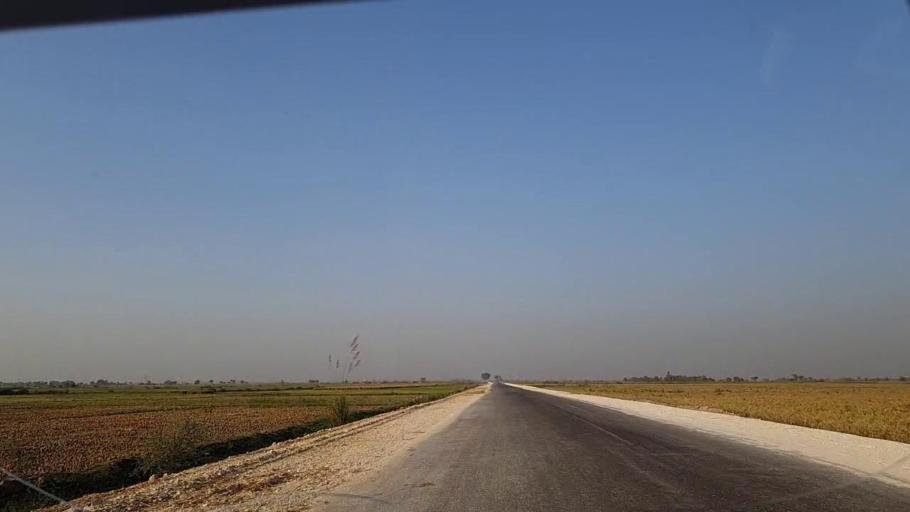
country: PK
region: Sindh
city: Rustam jo Goth
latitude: 27.9796
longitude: 68.8059
